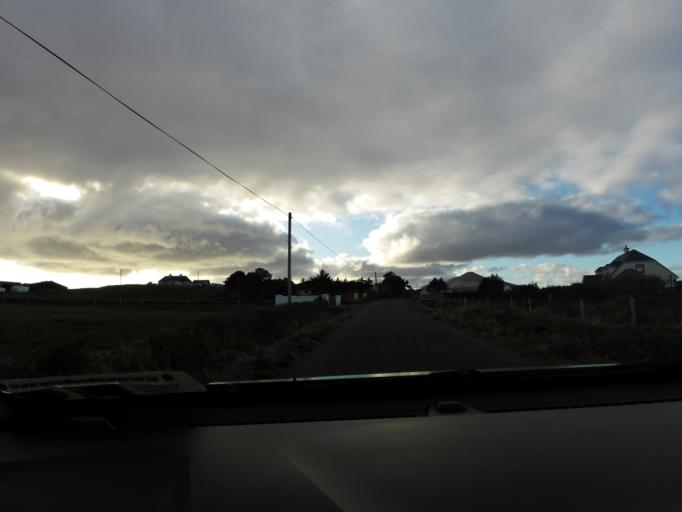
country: IE
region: Connaught
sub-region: Maigh Eo
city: Belmullet
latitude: 53.9952
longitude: -9.9442
